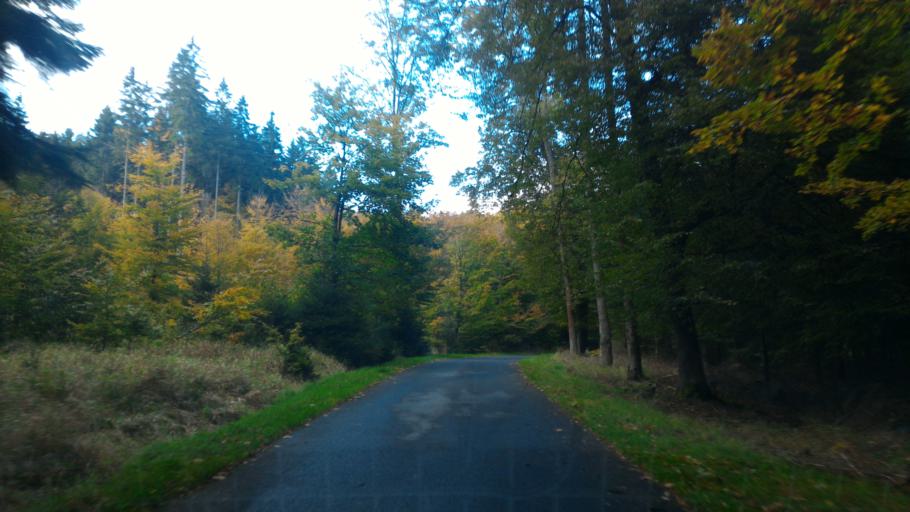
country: CZ
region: Ustecky
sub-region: Okres Decin
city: Chribska
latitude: 50.8230
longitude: 14.4887
